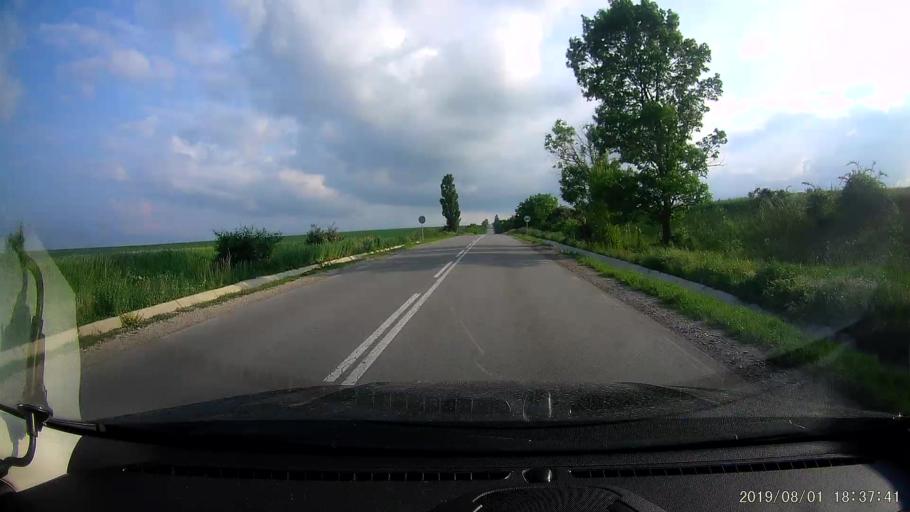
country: BG
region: Shumen
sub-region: Obshtina Khitrino
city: Gara Khitrino
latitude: 43.4162
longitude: 26.9271
